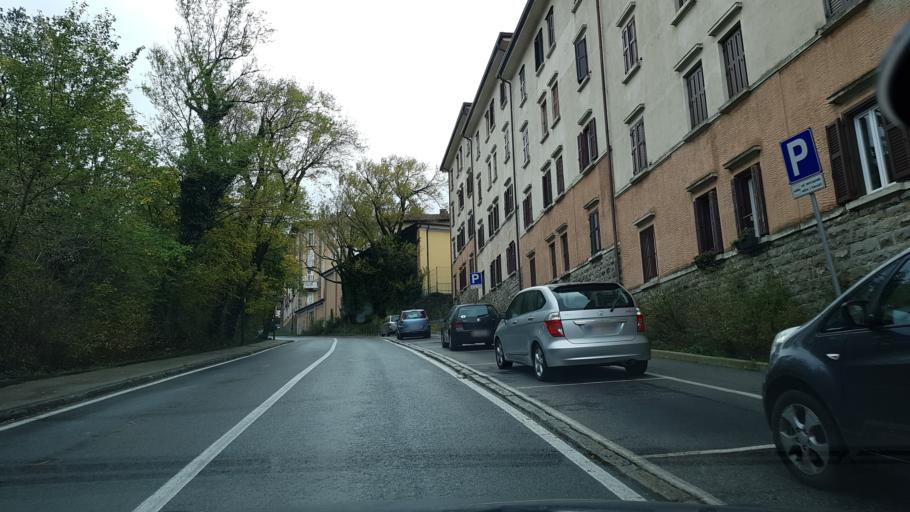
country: IT
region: Friuli Venezia Giulia
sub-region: Provincia di Trieste
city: Trieste
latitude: 45.6522
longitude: 13.7925
